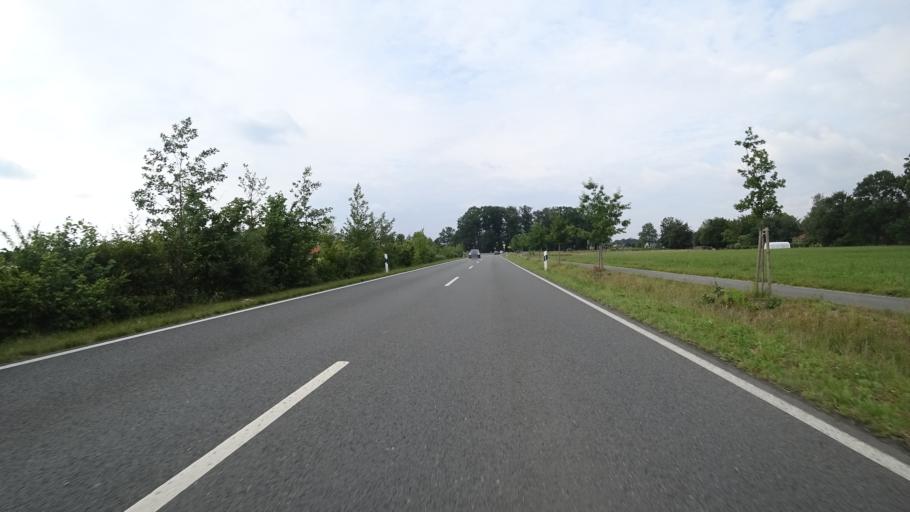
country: DE
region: North Rhine-Westphalia
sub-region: Regierungsbezirk Detmold
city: Guetersloh
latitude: 51.9540
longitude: 8.3802
